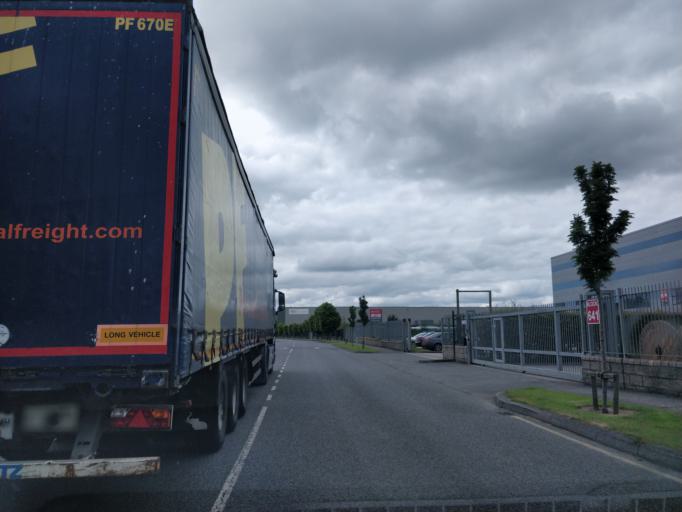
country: IE
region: Leinster
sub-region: South Dublin
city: Rathcoole
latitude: 53.2961
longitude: -6.4654
